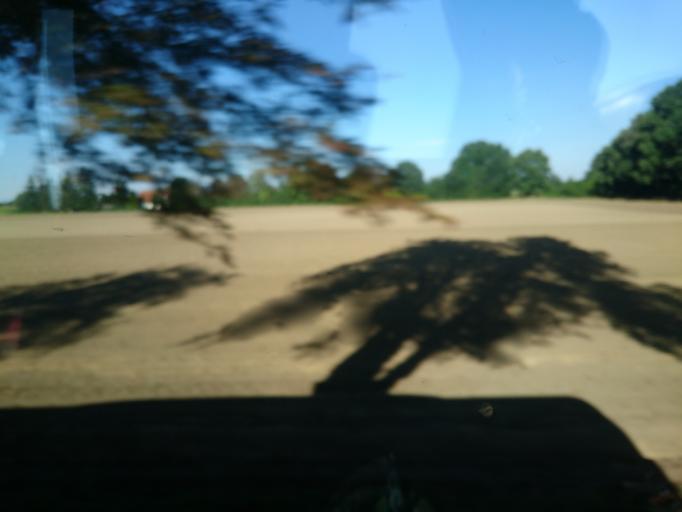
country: DE
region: Mecklenburg-Vorpommern
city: Ducherow
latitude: 53.7348
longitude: 13.7972
